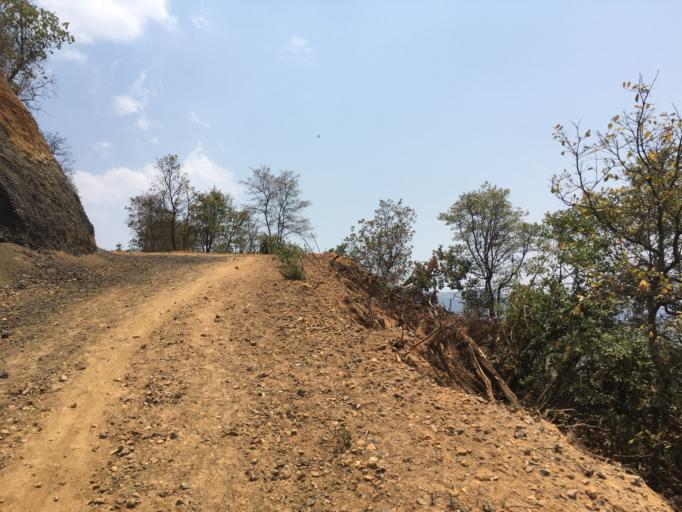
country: MX
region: Michoacan
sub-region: Patzcuaro
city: Santa Ana Chapitiro
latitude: 19.5135
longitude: -101.6442
